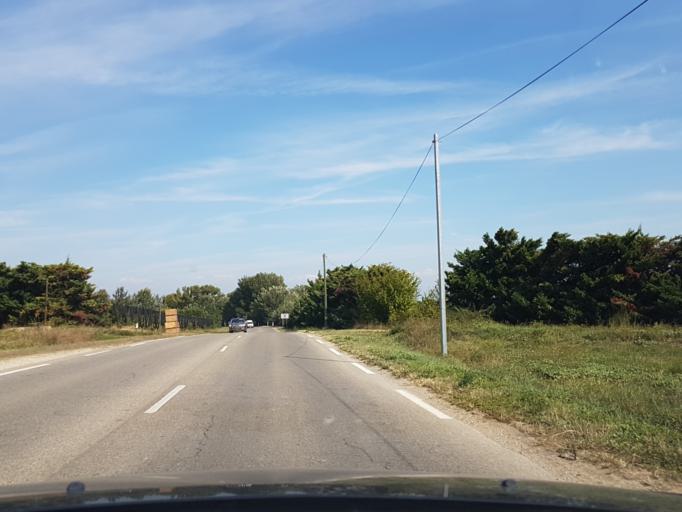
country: FR
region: Provence-Alpes-Cote d'Azur
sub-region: Departement des Bouches-du-Rhone
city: Eyragues
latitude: 43.8174
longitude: 4.8766
